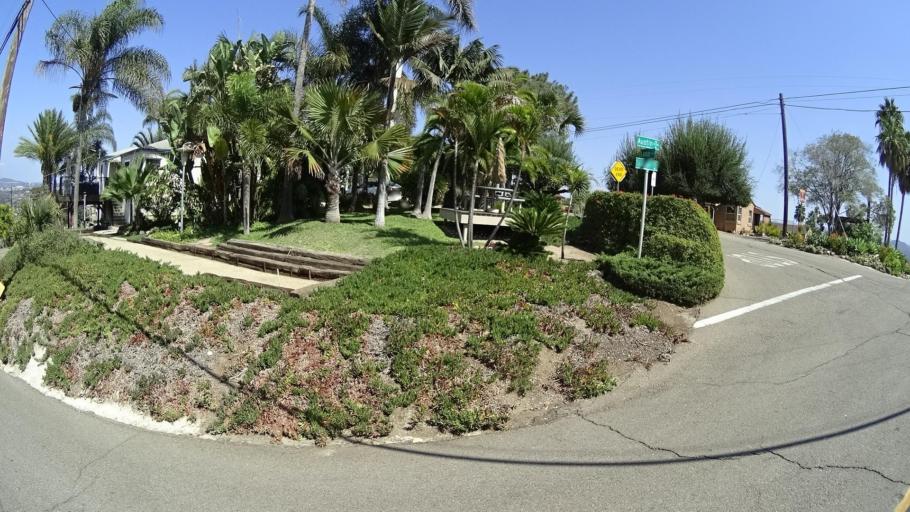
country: US
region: California
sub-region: San Diego County
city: Spring Valley
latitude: 32.7335
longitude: -116.9911
